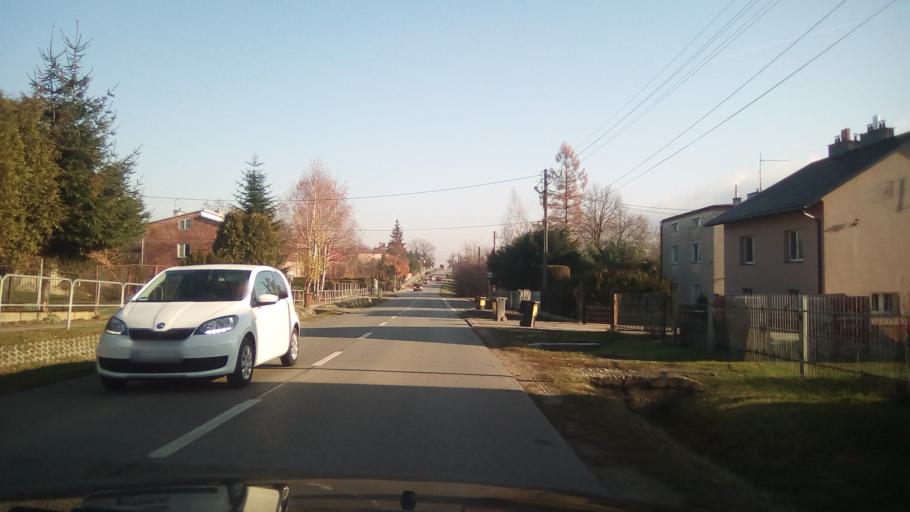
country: PL
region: Subcarpathian Voivodeship
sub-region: Rzeszow
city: Przybyszowka
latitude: 50.0423
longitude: 21.9133
